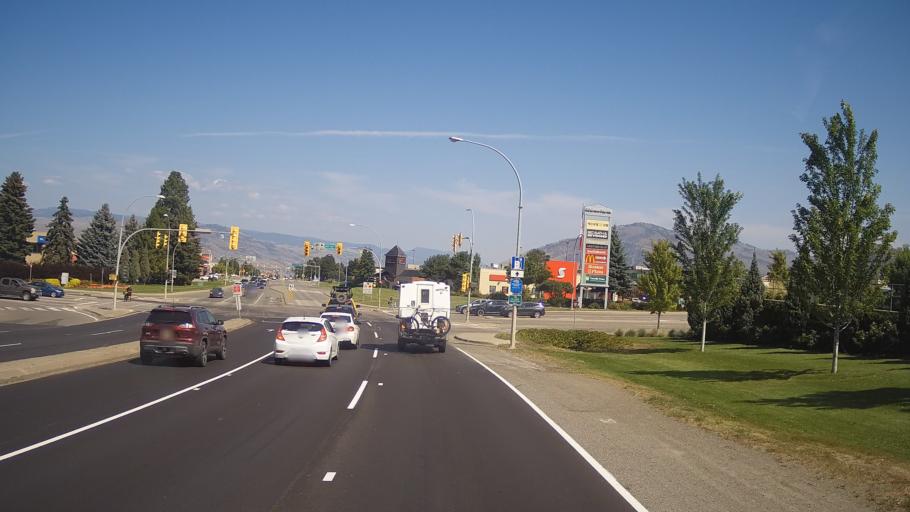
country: CA
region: British Columbia
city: Kamloops
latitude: 50.6630
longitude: -120.3538
